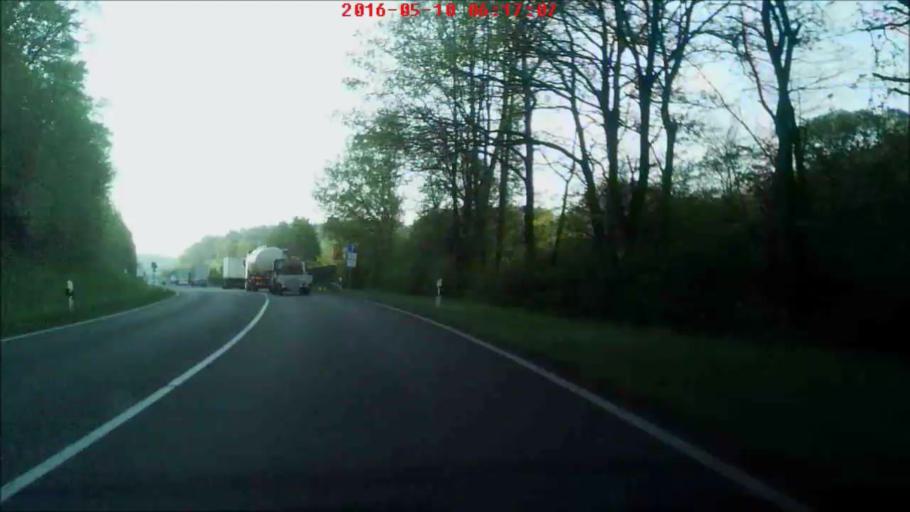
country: DE
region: Hesse
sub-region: Regierungsbezirk Kassel
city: Burghaun
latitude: 50.7374
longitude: 9.6925
